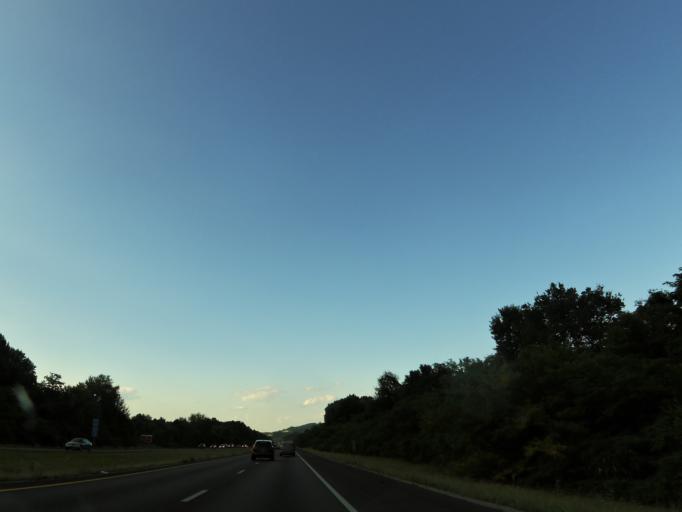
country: US
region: Tennessee
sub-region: Williamson County
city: Thompson's Station
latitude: 35.7970
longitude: -86.8571
